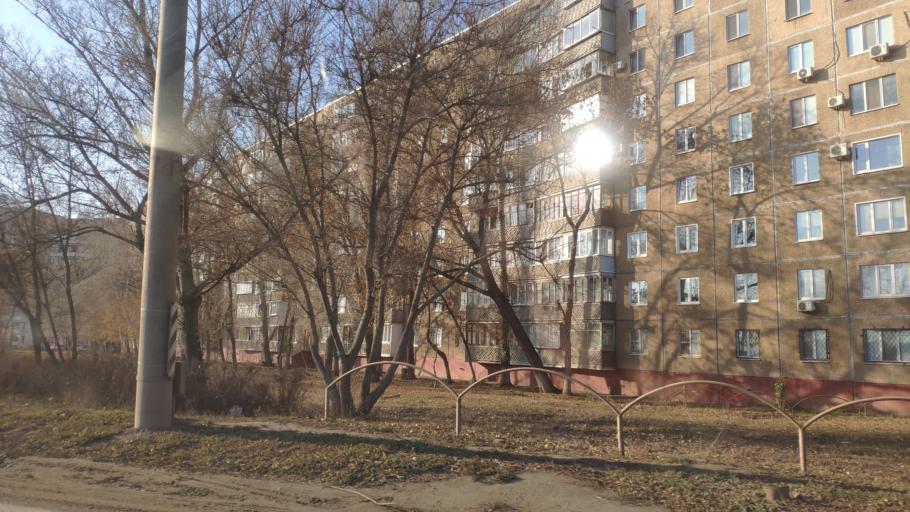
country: RU
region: Orenburg
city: Prigorodnyy
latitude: 51.7767
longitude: 55.1918
